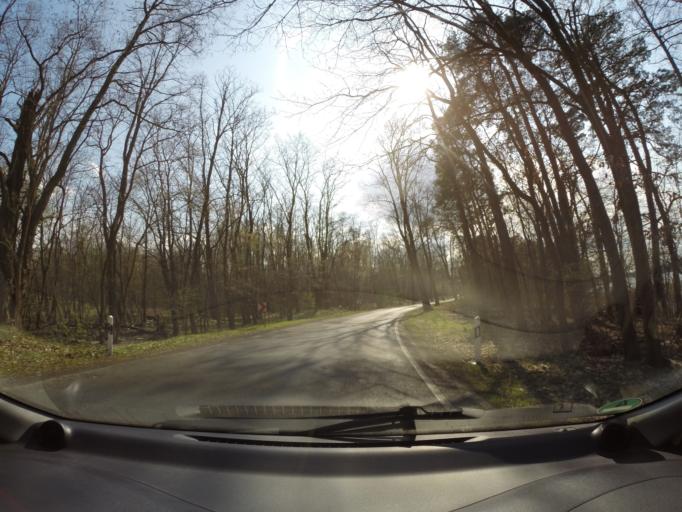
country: DE
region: Brandenburg
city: Rehfelde
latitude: 52.4679
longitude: 13.9558
